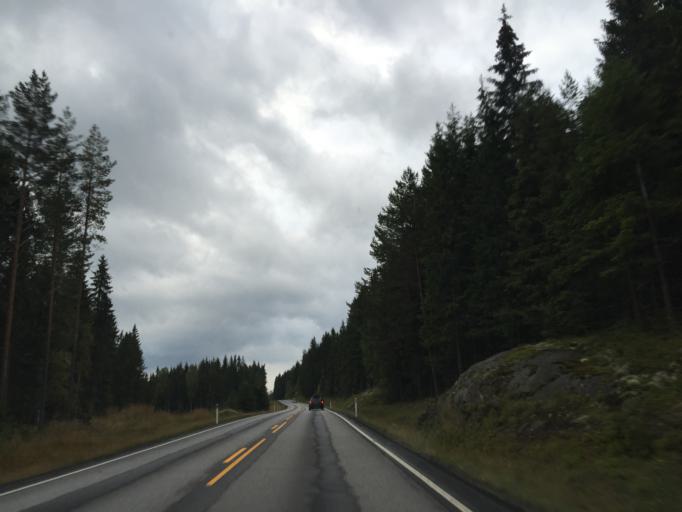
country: NO
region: Hedmark
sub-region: Nord-Odal
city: Sand
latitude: 60.4721
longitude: 11.5068
